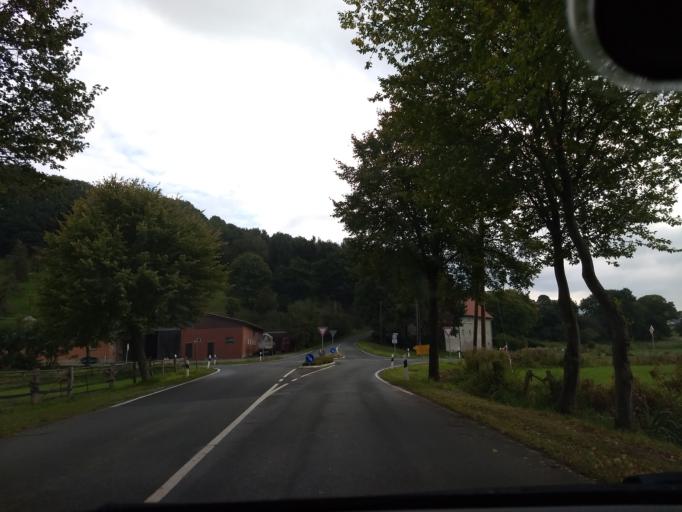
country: DE
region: North Rhine-Westphalia
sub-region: Regierungsbezirk Detmold
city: Buren
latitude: 51.5242
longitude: 8.5327
